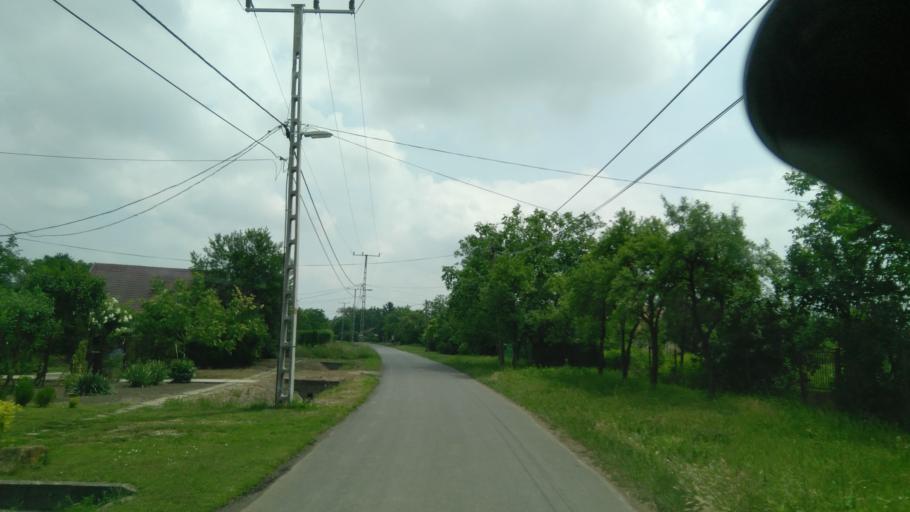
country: HU
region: Bekes
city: Gyula
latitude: 46.6592
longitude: 21.2520
